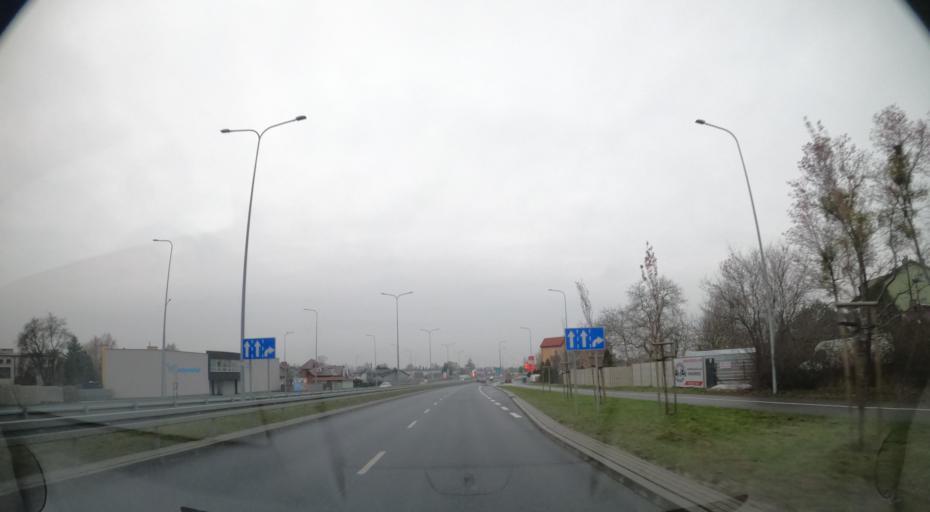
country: PL
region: Masovian Voivodeship
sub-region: Radom
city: Radom
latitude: 51.3839
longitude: 21.1848
